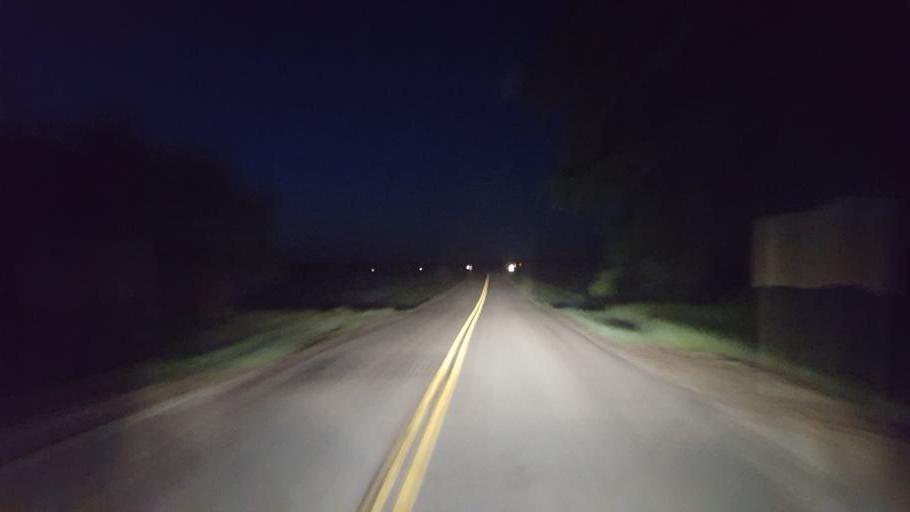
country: US
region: Iowa
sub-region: Decatur County
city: Lamoni
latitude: 40.4374
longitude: -93.8157
